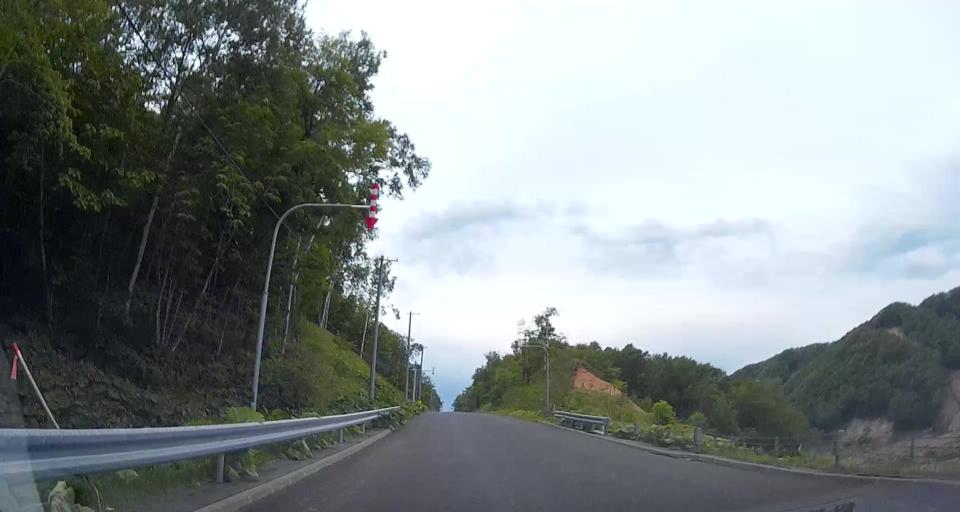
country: JP
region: Hokkaido
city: Chitose
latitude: 42.7824
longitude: 142.0193
